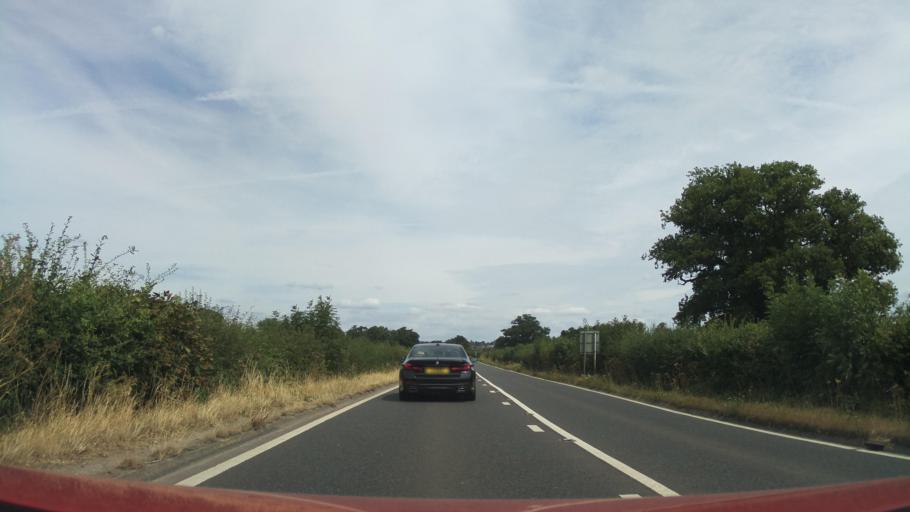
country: GB
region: England
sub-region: Surrey
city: Salfords
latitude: 51.2011
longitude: -0.1984
